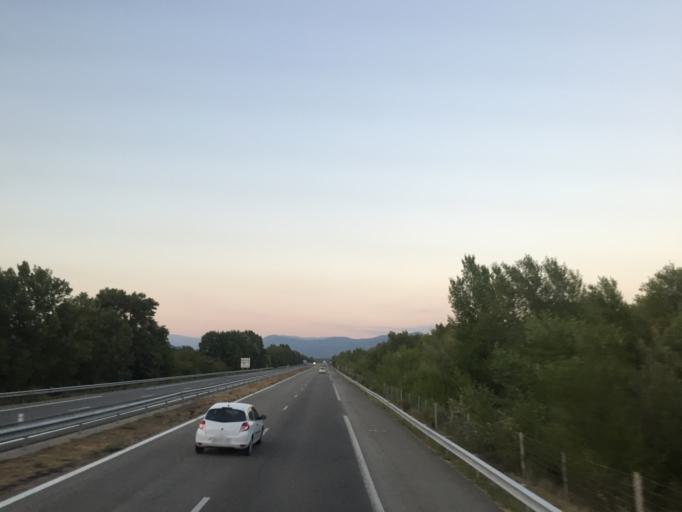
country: FR
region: Provence-Alpes-Cote d'Azur
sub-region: Departement des Alpes-de-Haute-Provence
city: Peyruis
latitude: 44.0130
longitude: 5.9375
